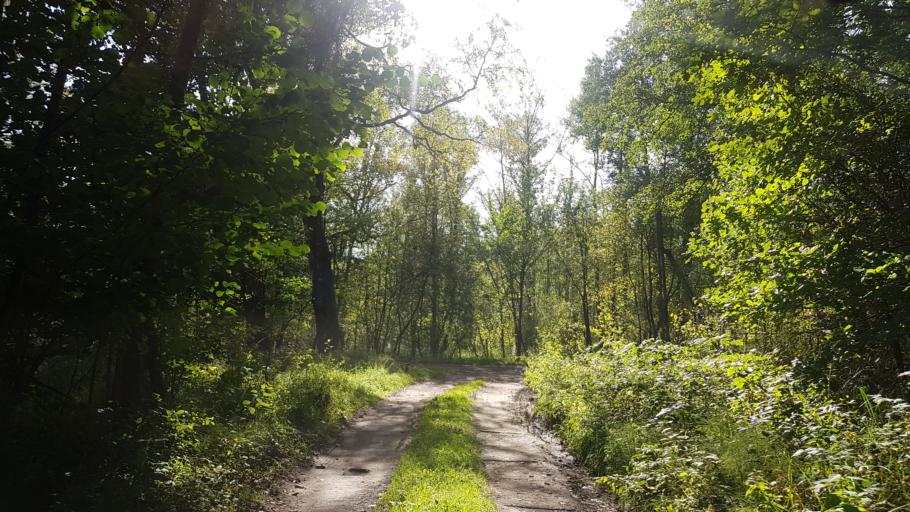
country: PL
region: West Pomeranian Voivodeship
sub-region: Powiat koszalinski
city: Polanow
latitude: 54.0540
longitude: 16.6157
